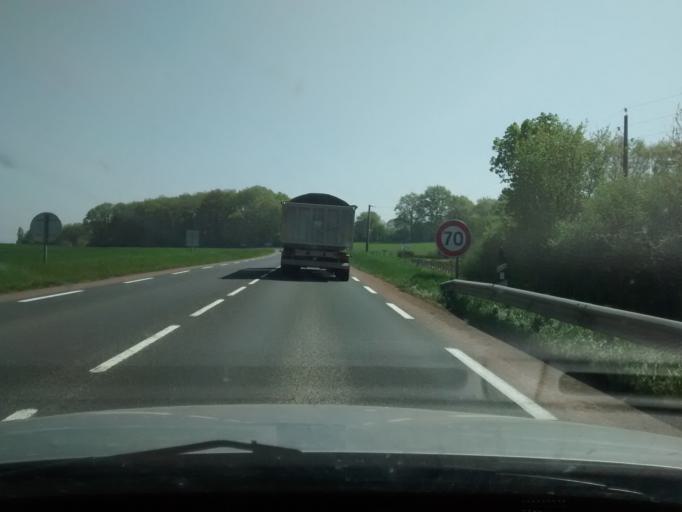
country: FR
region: Pays de la Loire
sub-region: Departement de la Sarthe
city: Loue
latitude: 48.0208
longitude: -0.0961
